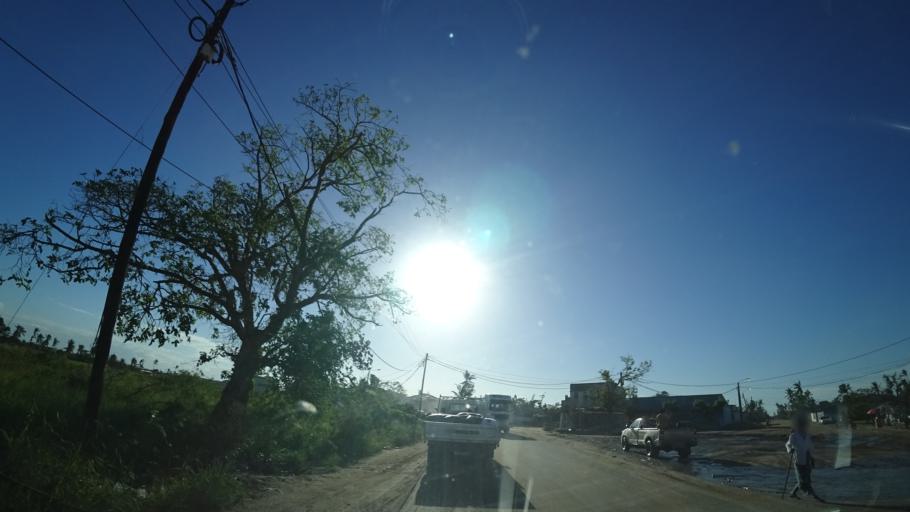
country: MZ
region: Sofala
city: Beira
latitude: -19.7805
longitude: 34.8753
